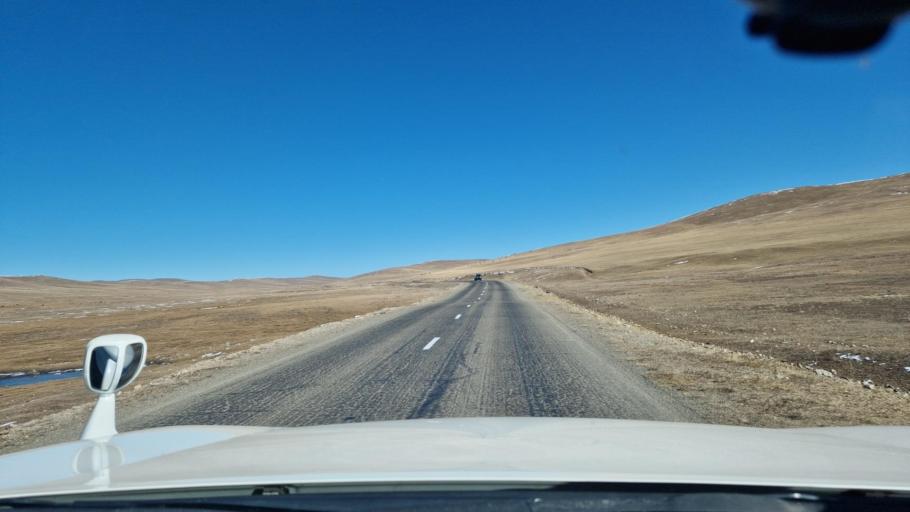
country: MN
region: Hentiy
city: Modot
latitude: 47.7665
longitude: 108.6457
